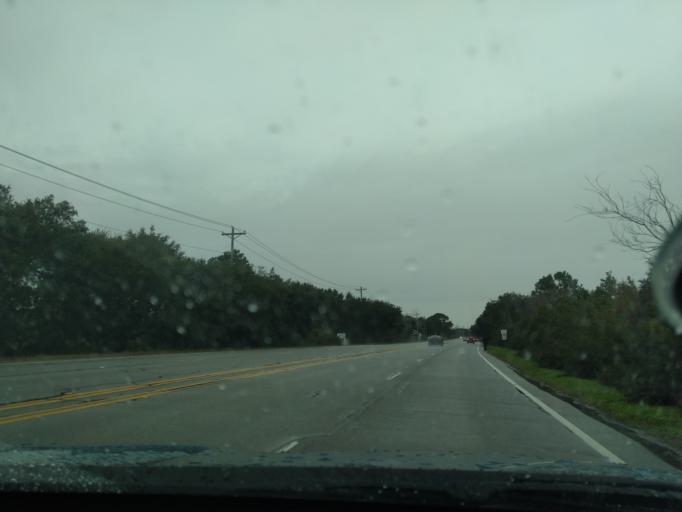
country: US
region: South Carolina
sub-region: Charleston County
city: Folly Beach
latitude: 32.6905
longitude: -79.9629
